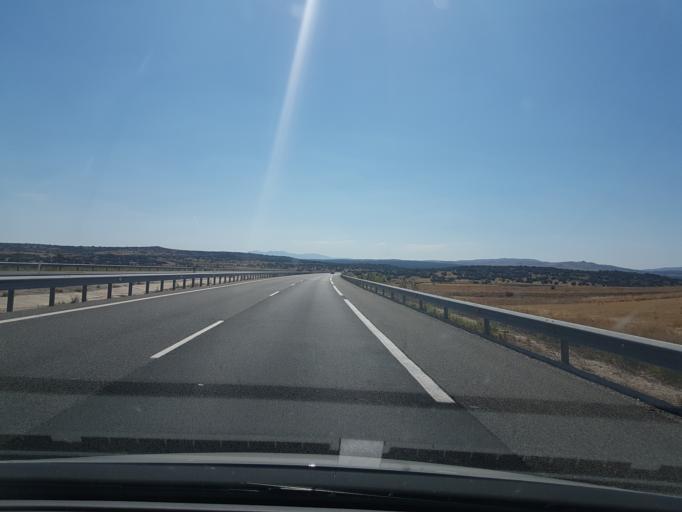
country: ES
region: Castille and Leon
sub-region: Provincia de Avila
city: Cardenosa
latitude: 40.7547
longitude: -4.7561
